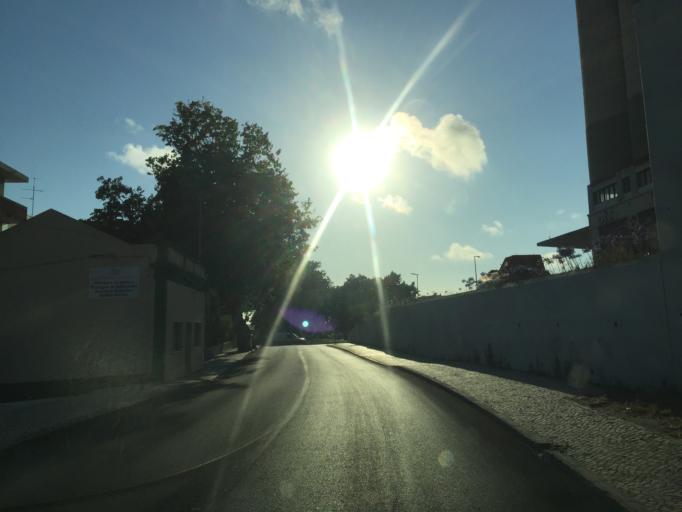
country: PT
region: Leiria
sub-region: Caldas da Rainha
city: Caldas da Rainha
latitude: 39.4019
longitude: -9.1390
